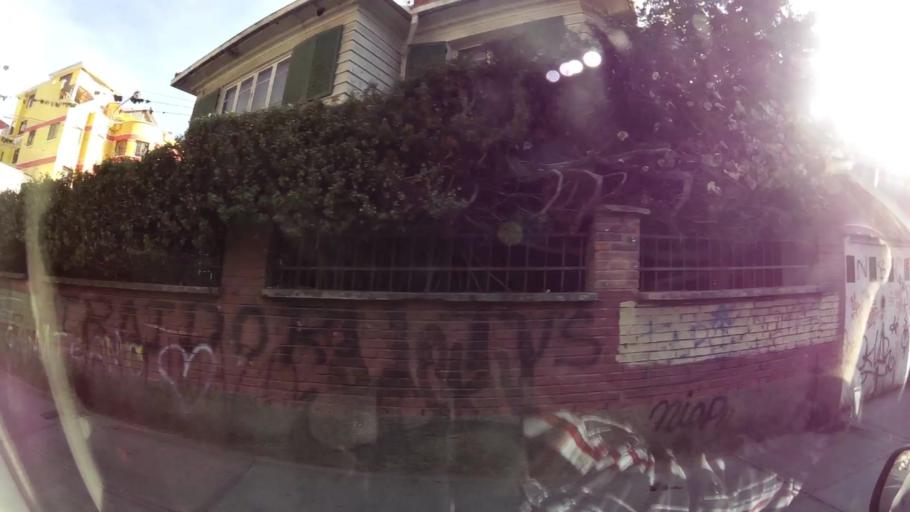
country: BO
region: La Paz
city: La Paz
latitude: -16.5026
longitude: -68.1194
